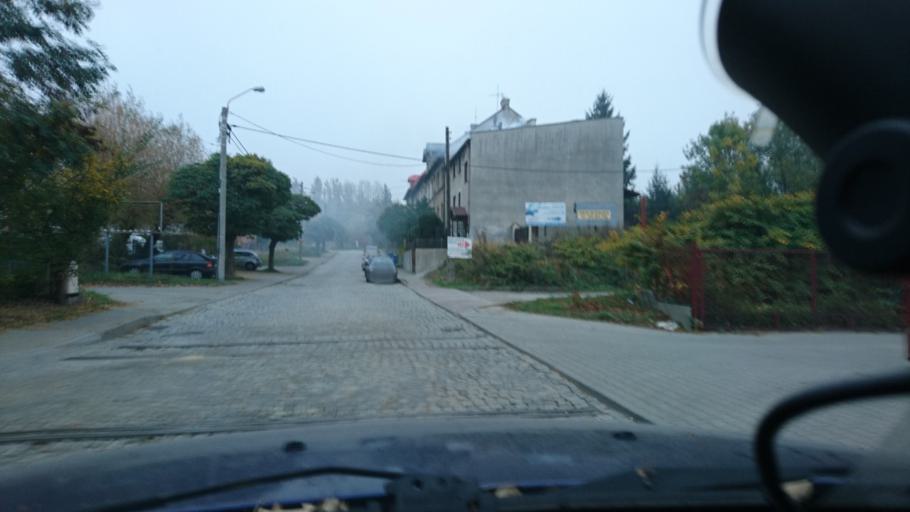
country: PL
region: Silesian Voivodeship
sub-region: Bielsko-Biala
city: Bielsko-Biala
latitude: 49.8303
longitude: 19.0609
